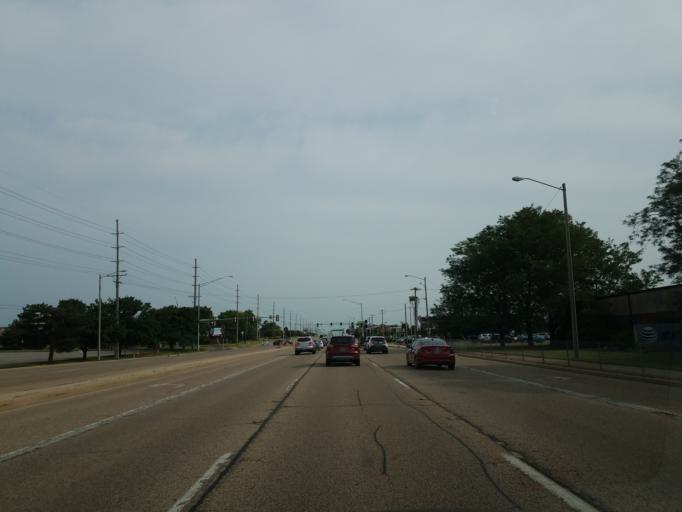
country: US
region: Illinois
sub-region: McLean County
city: Bloomington
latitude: 40.4787
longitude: -88.9525
